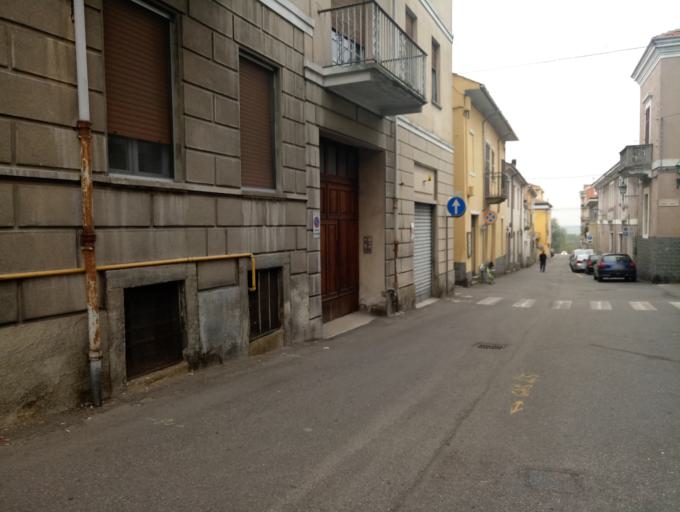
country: IT
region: Piedmont
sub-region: Provincia di Alessandria
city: Valenza
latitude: 45.0153
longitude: 8.6448
